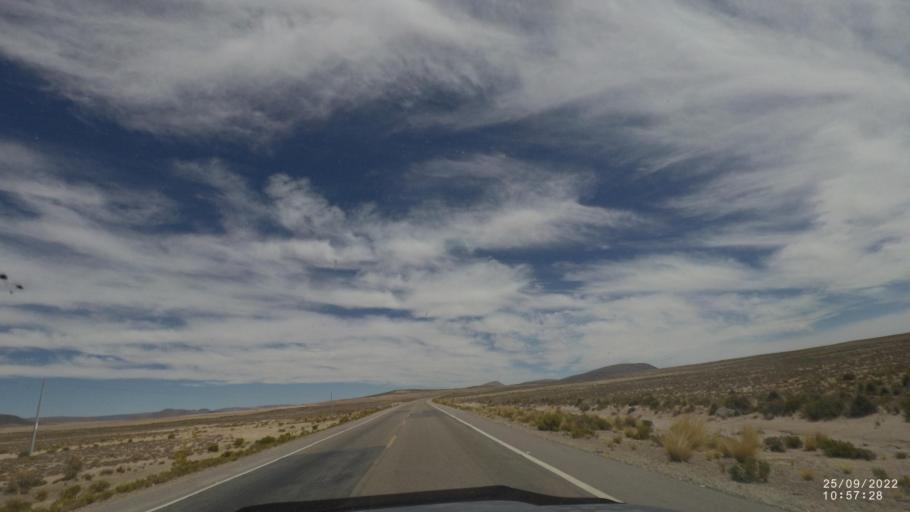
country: BO
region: Oruro
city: Challapata
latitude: -19.4747
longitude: -66.8915
